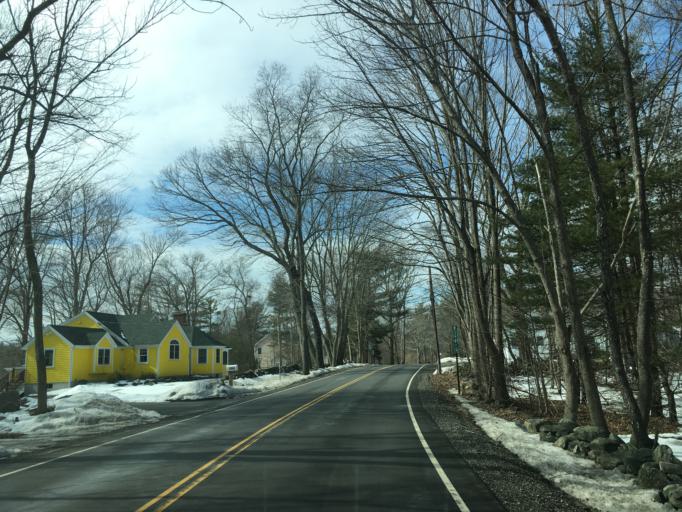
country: US
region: New Hampshire
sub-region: Rockingham County
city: North Hampton
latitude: 42.9896
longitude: -70.8767
